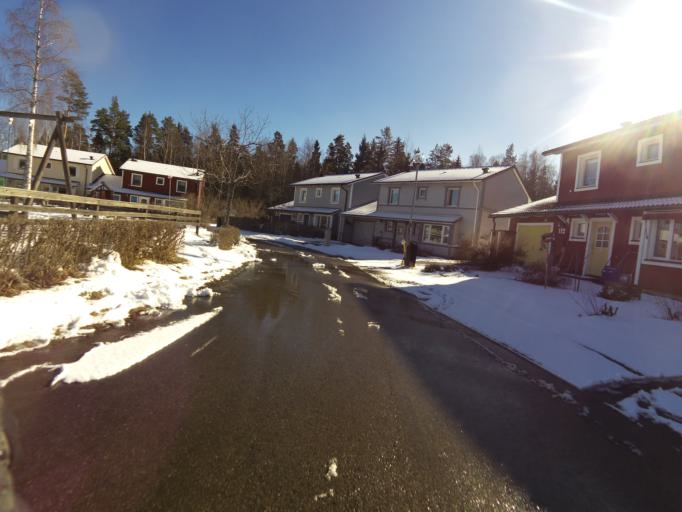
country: SE
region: Gaevleborg
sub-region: Gavle Kommun
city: Gavle
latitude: 60.6609
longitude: 17.2267
